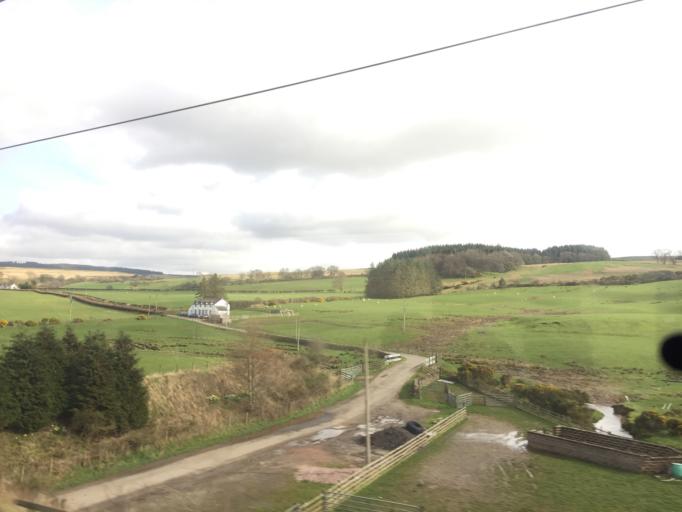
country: GB
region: Scotland
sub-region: Dumfries and Galloway
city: Lochmaben
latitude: 55.2085
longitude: -3.3994
